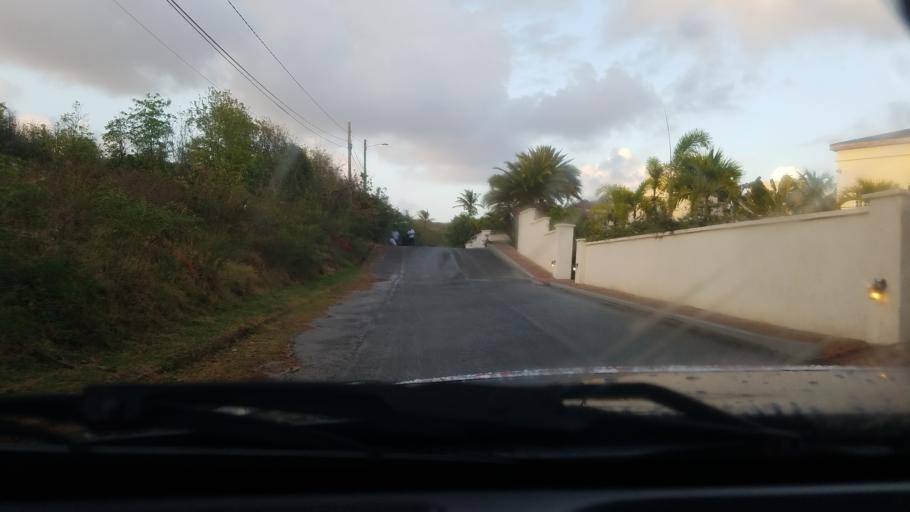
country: LC
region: Gros-Islet
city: Gros Islet
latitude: 14.0908
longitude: -60.9313
